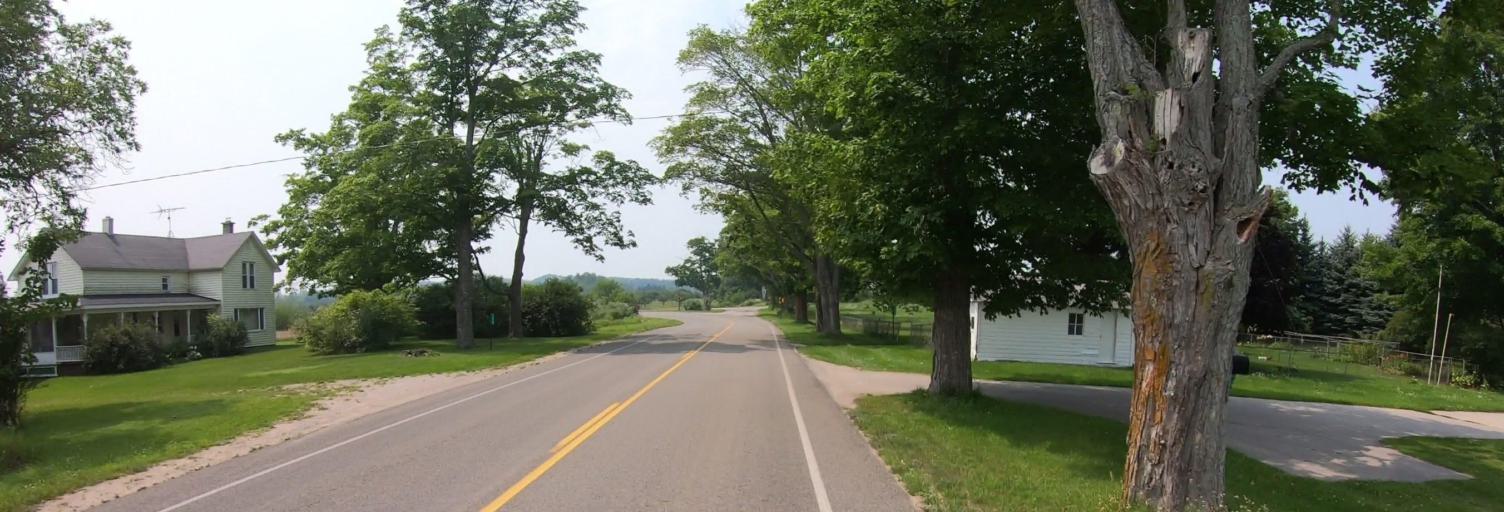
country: US
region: Michigan
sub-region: Leelanau County
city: Leland
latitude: 45.1520
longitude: -85.6079
